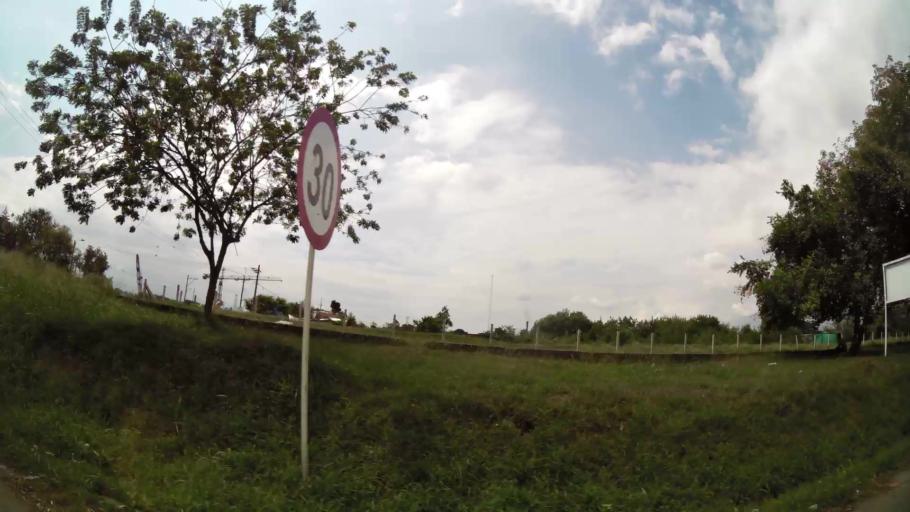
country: CO
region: Valle del Cauca
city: Cali
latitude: 3.4929
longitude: -76.4816
